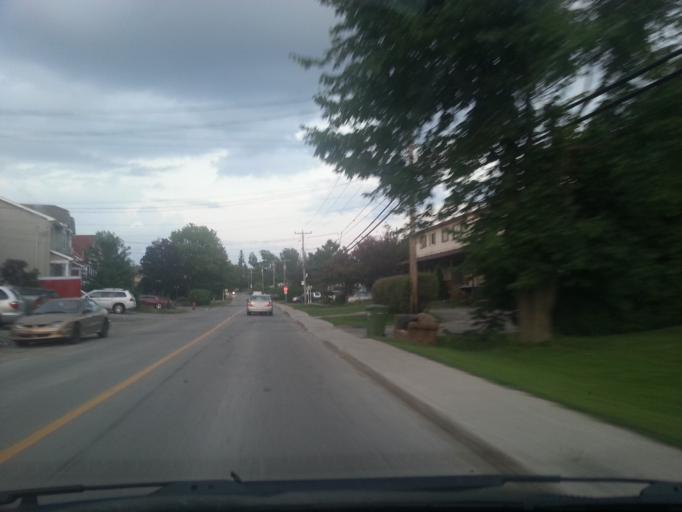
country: CA
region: Quebec
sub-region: Outaouais
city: Gatineau
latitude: 45.4989
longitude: -75.6188
